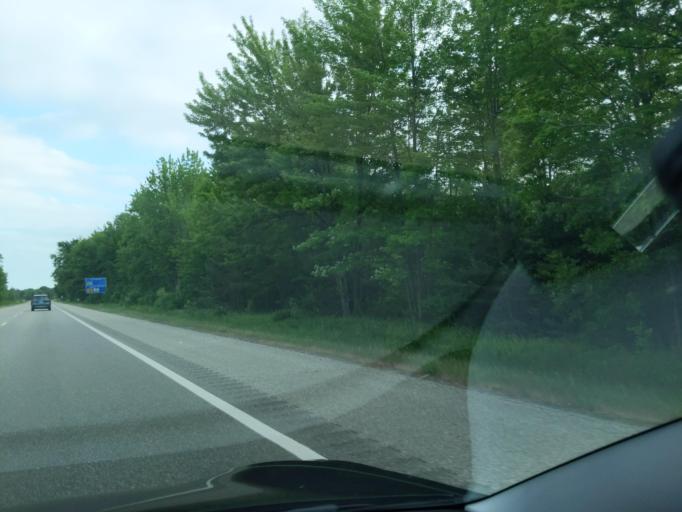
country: US
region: Michigan
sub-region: Muskegon County
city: Lakewood Club
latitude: 43.3337
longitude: -86.2440
